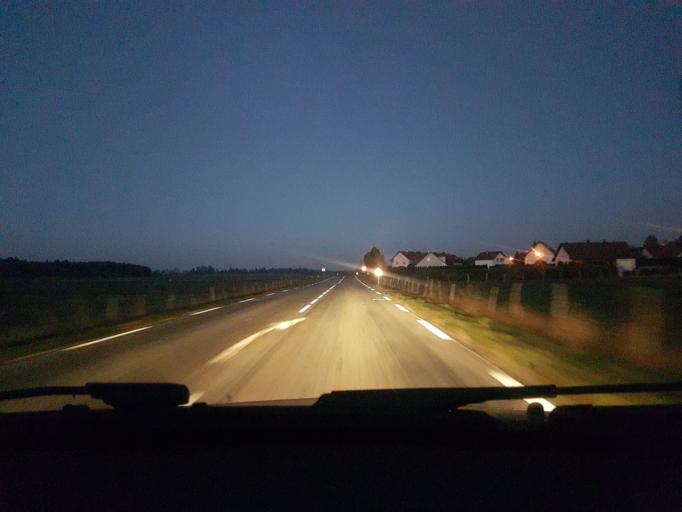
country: FR
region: Franche-Comte
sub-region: Departement du Doubs
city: Villers-le-Lac
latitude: 47.1071
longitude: 6.6757
